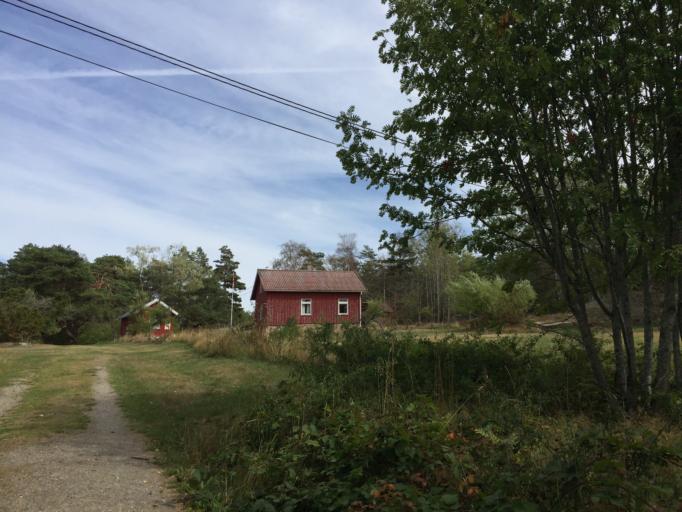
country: NO
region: Ostfold
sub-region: Fredrikstad
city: Fredrikstad
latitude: 59.0994
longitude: 10.9266
